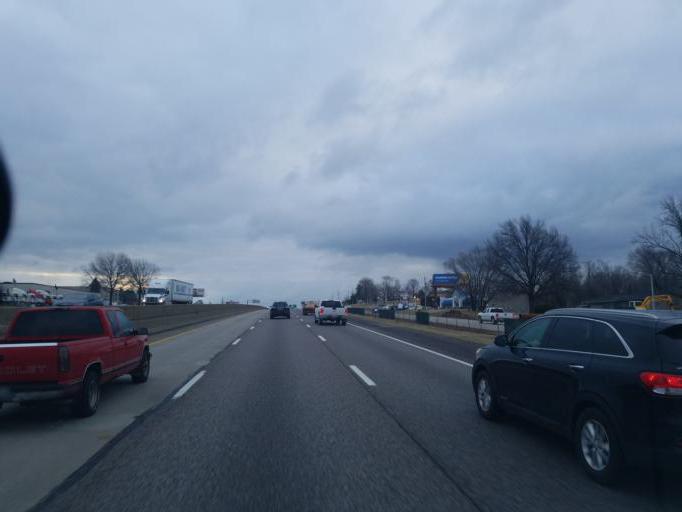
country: US
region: Missouri
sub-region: Saint Charles County
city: Lake Saint Louis
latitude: 38.8035
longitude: -90.7569
